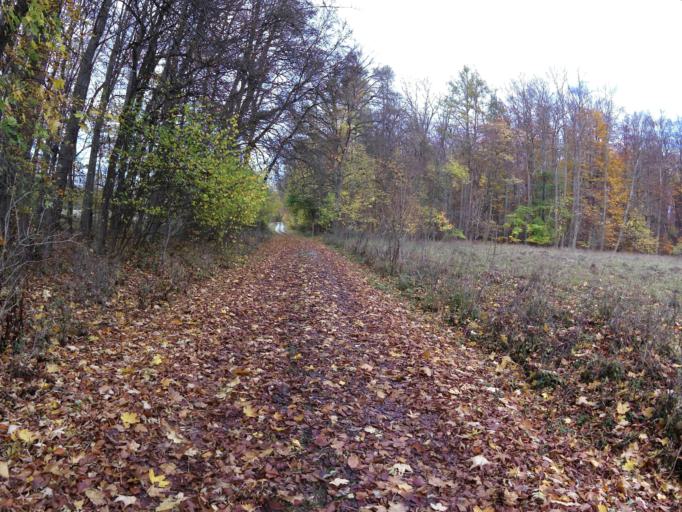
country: DE
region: Thuringia
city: Kammerforst
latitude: 51.0834
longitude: 10.4034
